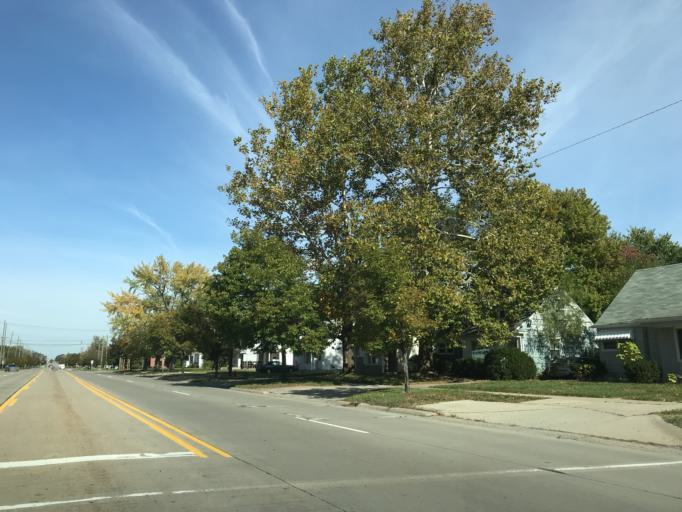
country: US
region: Michigan
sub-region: Oakland County
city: Farmington
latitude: 42.4615
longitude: -83.3567
